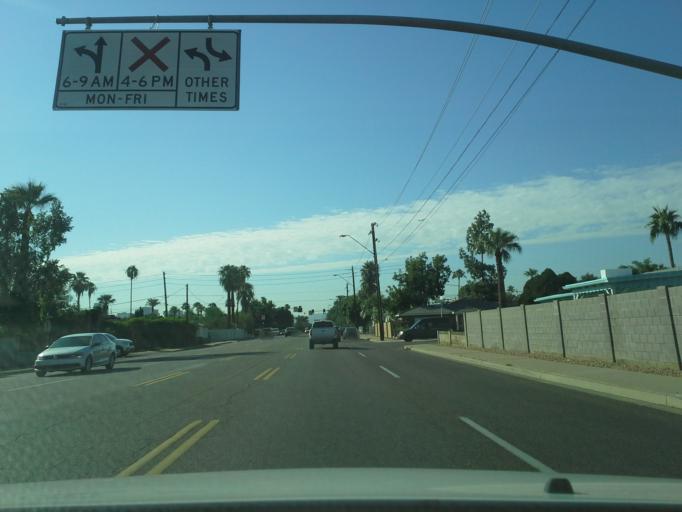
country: US
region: Arizona
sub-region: Maricopa County
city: Phoenix
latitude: 33.4746
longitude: -112.0829
